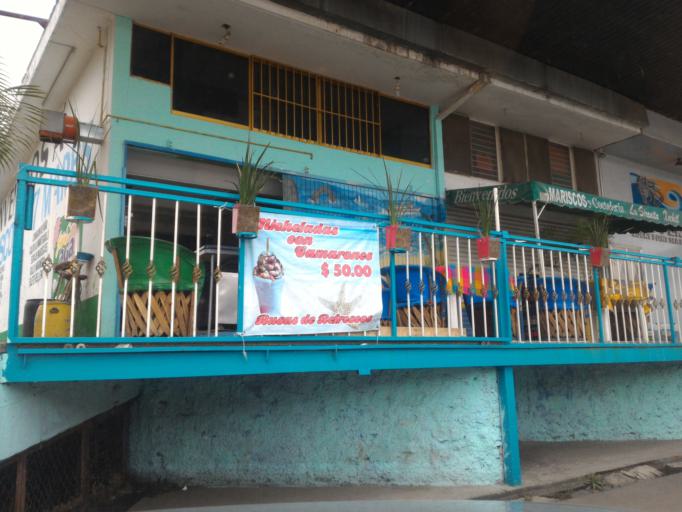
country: MX
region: Jalisco
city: Tlaquepaque
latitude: 20.6258
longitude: -103.3460
